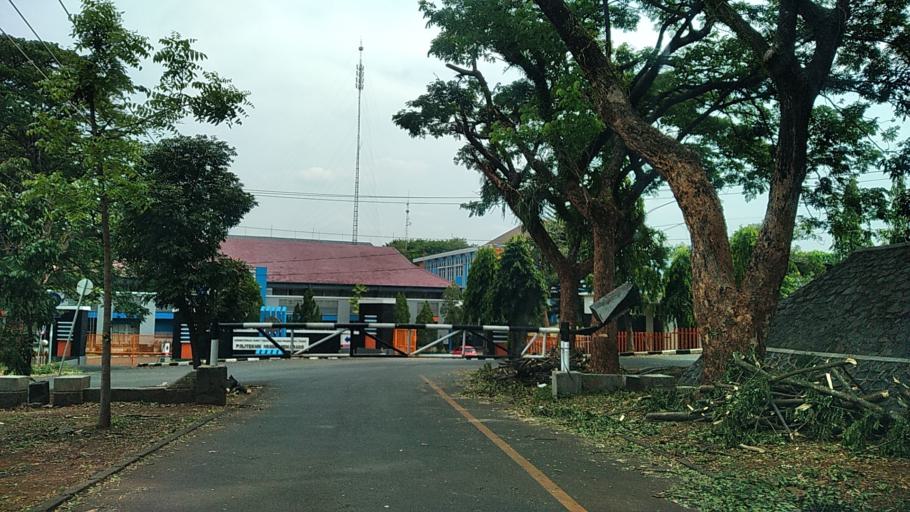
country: ID
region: Central Java
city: Semarang
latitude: -7.0513
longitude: 110.4356
